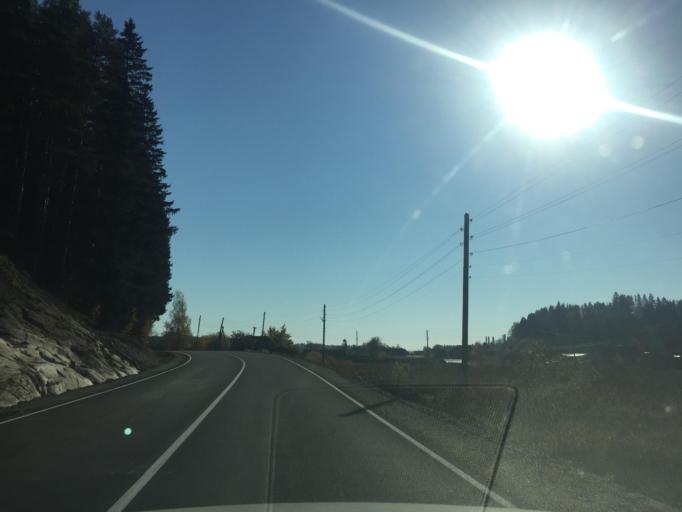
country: RU
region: Leningrad
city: Kuznechnoye
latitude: 61.3036
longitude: 29.8821
